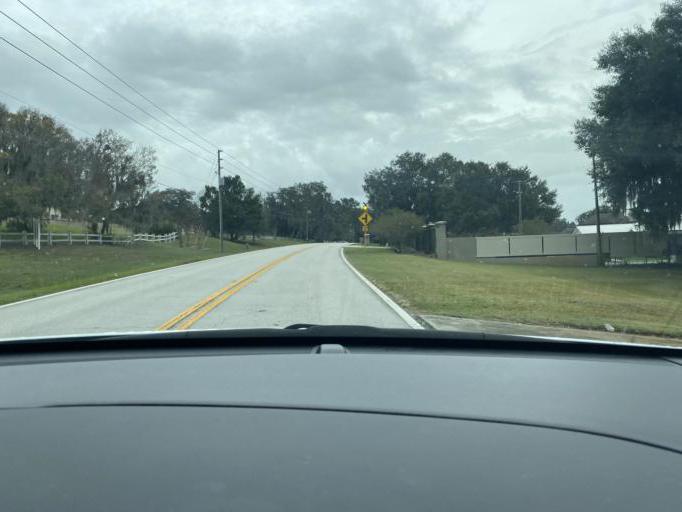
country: US
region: Florida
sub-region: Lake County
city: Minneola
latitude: 28.5892
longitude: -81.7726
